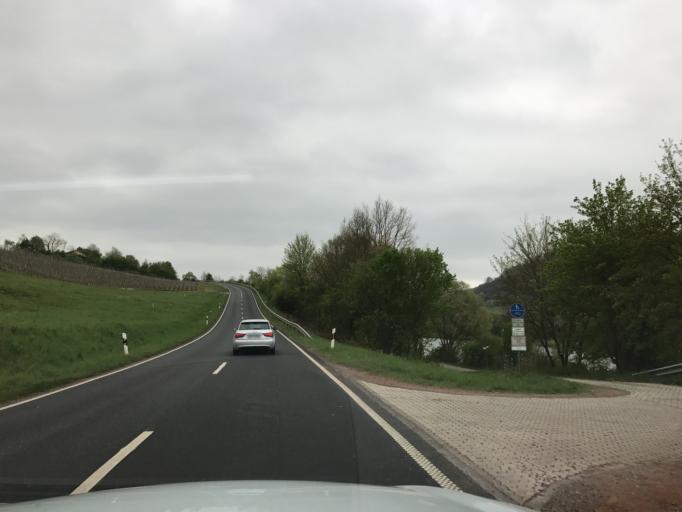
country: DE
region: Rheinland-Pfalz
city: Schoden
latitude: 49.6438
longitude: 6.5722
